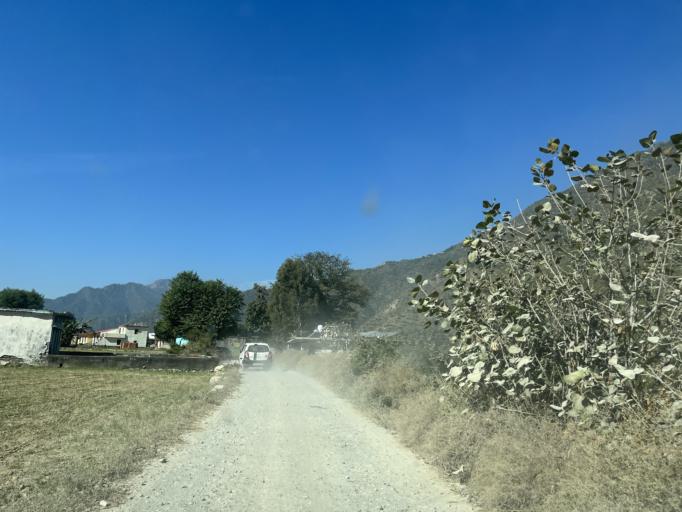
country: IN
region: Uttarakhand
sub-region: Almora
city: Ranikhet
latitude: 29.5520
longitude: 79.3883
